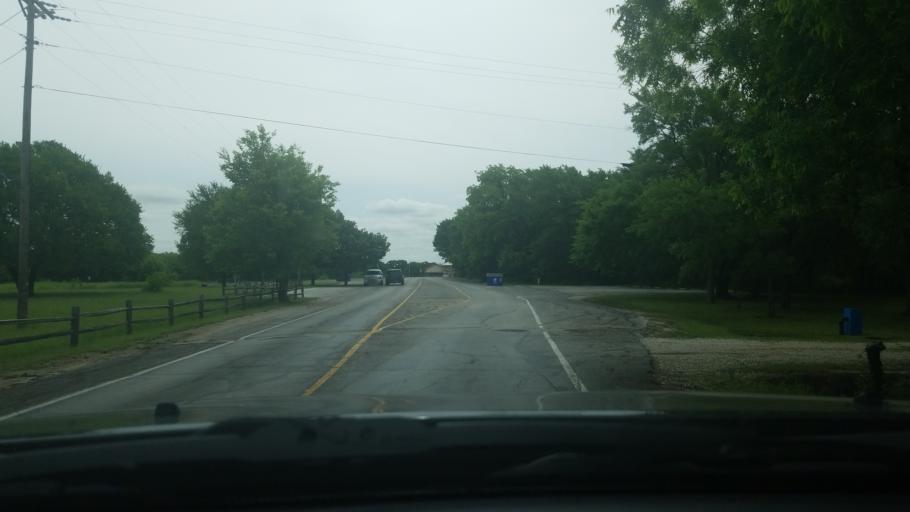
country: US
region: Texas
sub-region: Denton County
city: Lake Dallas
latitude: 33.1069
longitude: -97.0041
